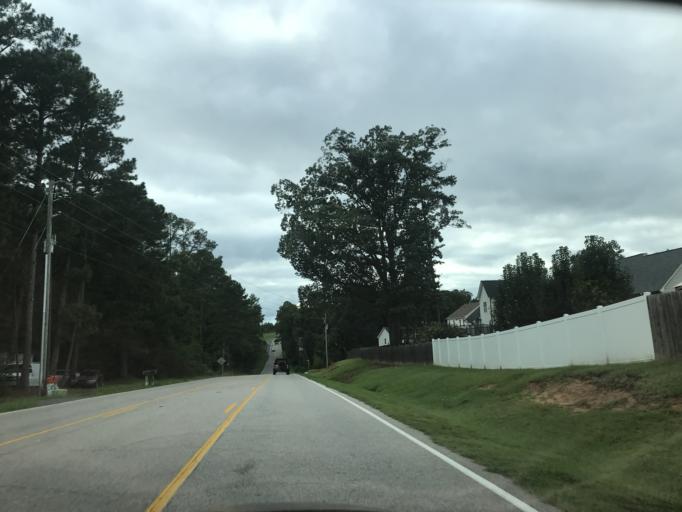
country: US
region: North Carolina
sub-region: Johnston County
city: Clayton
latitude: 35.5715
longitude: -78.5511
